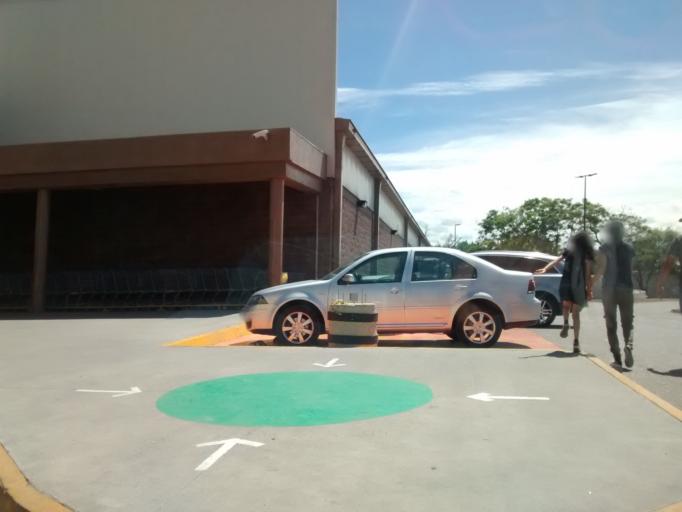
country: MX
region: Puebla
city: Tehuacan
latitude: 18.4673
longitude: -97.4155
